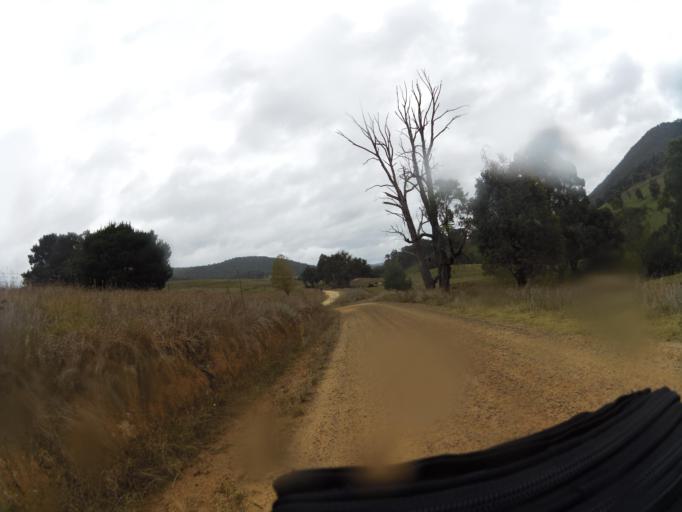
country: AU
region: New South Wales
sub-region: Greater Hume Shire
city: Holbrook
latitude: -36.2365
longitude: 147.6215
